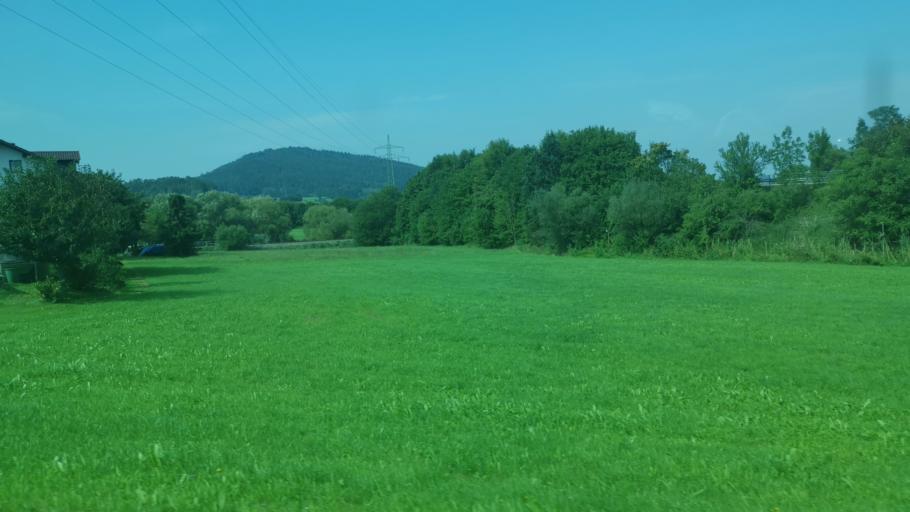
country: DE
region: Bavaria
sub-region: Upper Palatinate
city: Chamerau
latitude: 49.2026
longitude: 12.7548
